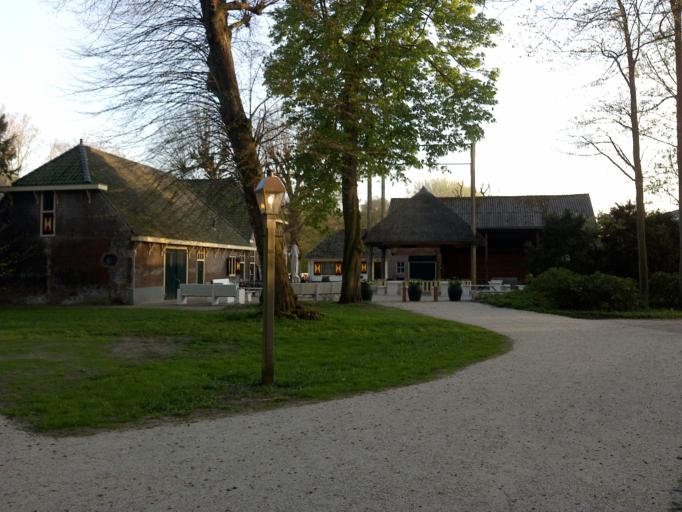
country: NL
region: South Holland
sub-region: Gemeente Lisse
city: Lisse
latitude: 52.2674
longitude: 4.5395
